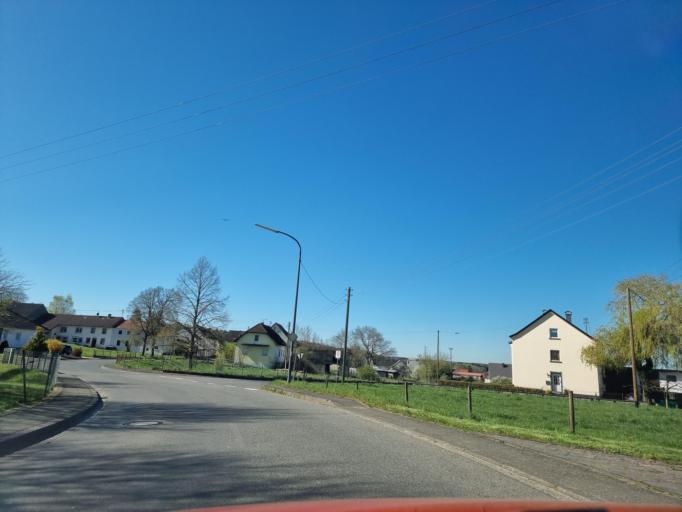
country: DE
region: Rheinland-Pfalz
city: Ernzen
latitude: 49.8439
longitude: 6.4283
